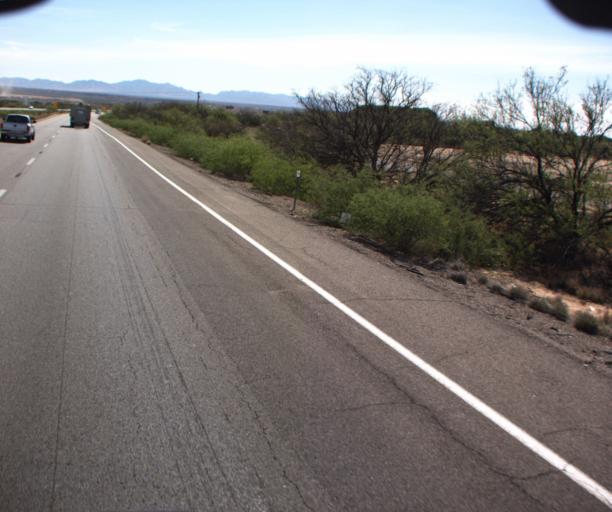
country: US
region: Arizona
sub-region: Cochise County
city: Benson
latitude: 31.9784
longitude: -110.3005
